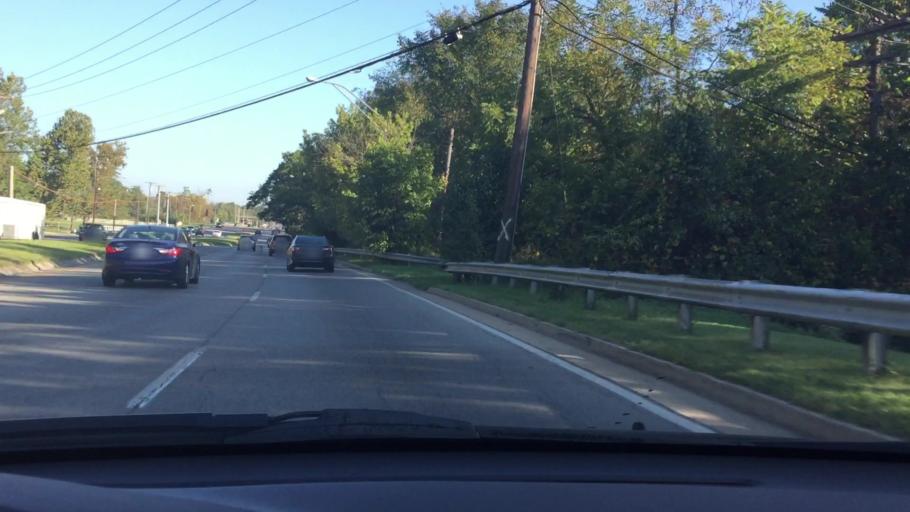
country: US
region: Kentucky
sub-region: Fayette County
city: Lexington
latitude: 37.9857
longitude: -84.4940
